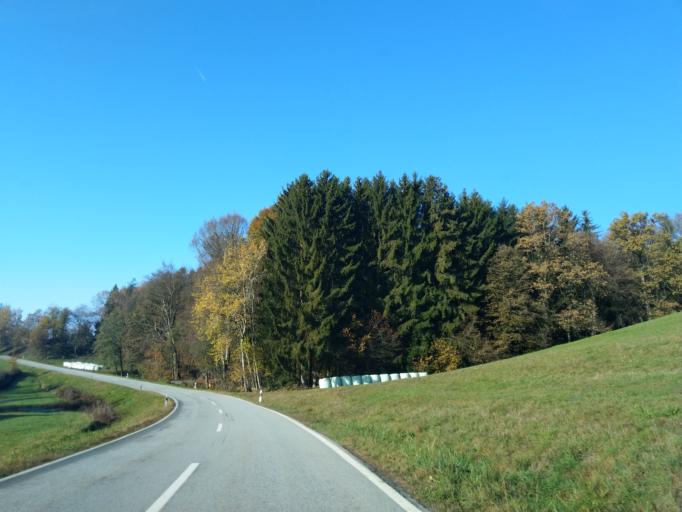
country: DE
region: Bavaria
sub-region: Lower Bavaria
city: Zenting
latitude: 48.7631
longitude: 13.2498
